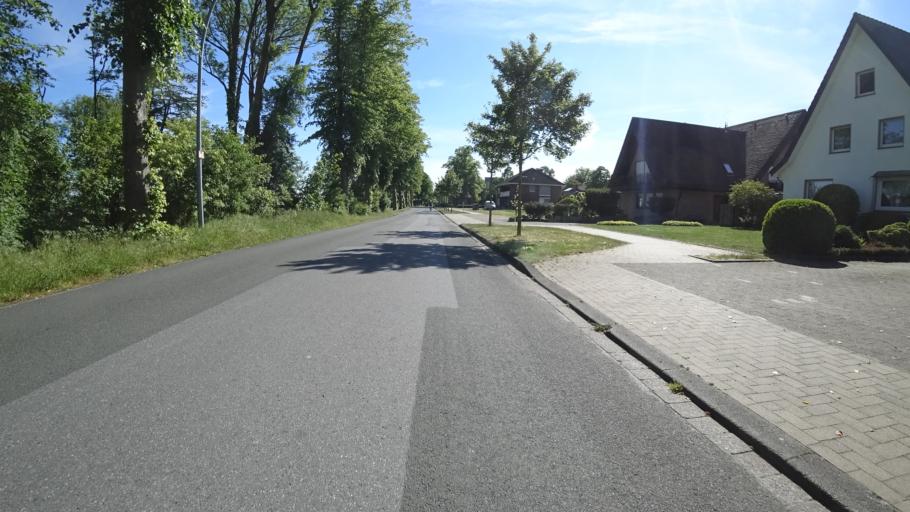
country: DE
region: North Rhine-Westphalia
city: Oelde
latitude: 51.8029
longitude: 8.2103
